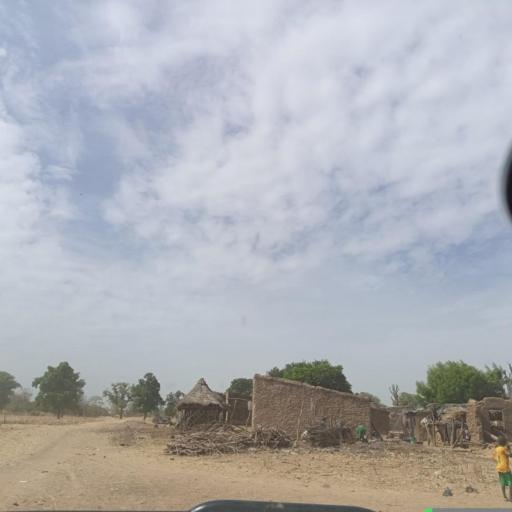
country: ML
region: Koulikoro
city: Koulikoro
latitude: 13.1670
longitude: -7.7870
